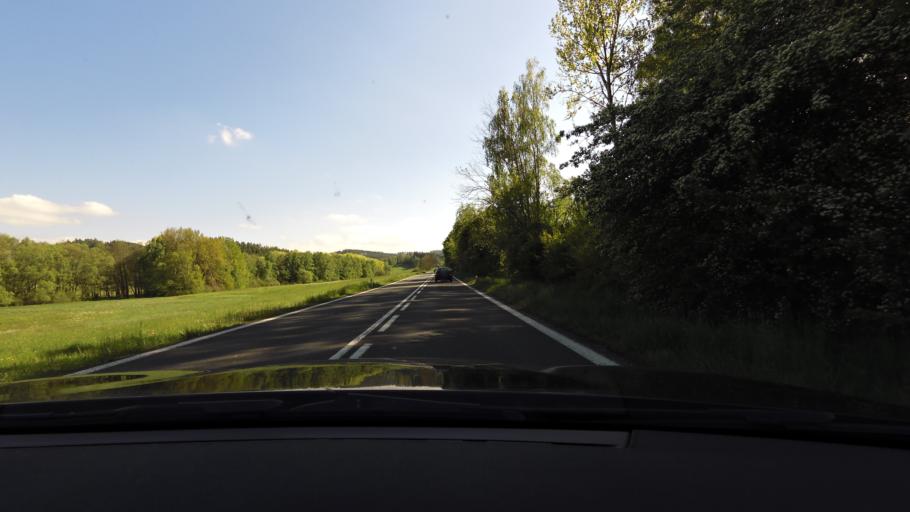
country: CZ
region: Plzensky
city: Strazov
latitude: 49.3215
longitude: 13.3007
